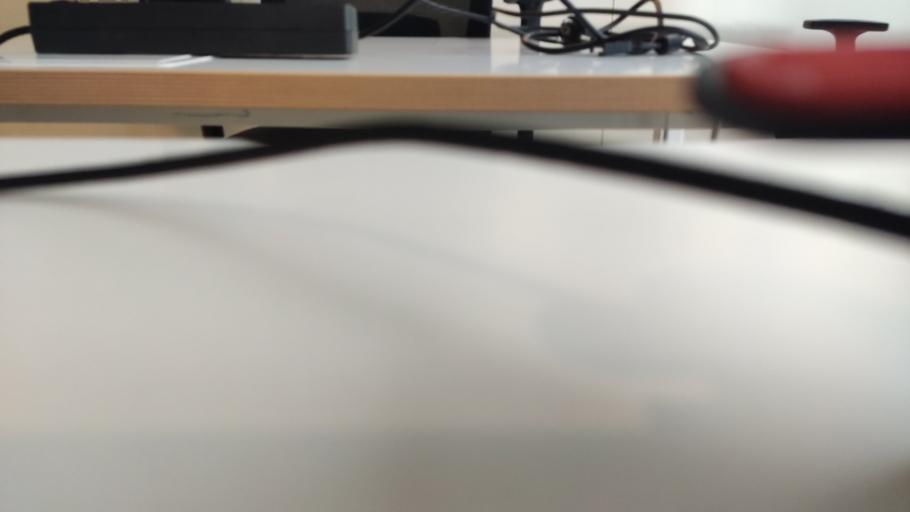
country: RU
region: Moskovskaya
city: Rogachevo
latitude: 56.4245
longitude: 37.1017
